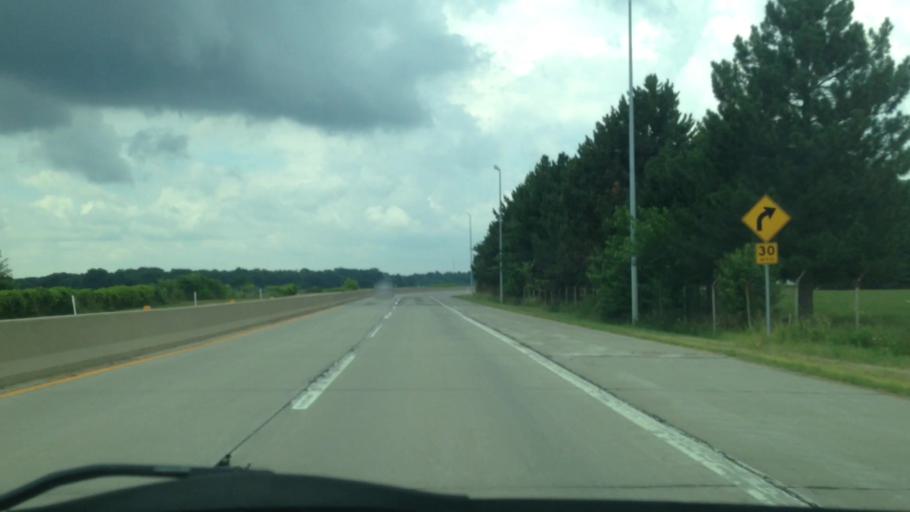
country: US
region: Indiana
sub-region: Saint Joseph County
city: Notre Dame
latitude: 41.7122
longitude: -86.2541
